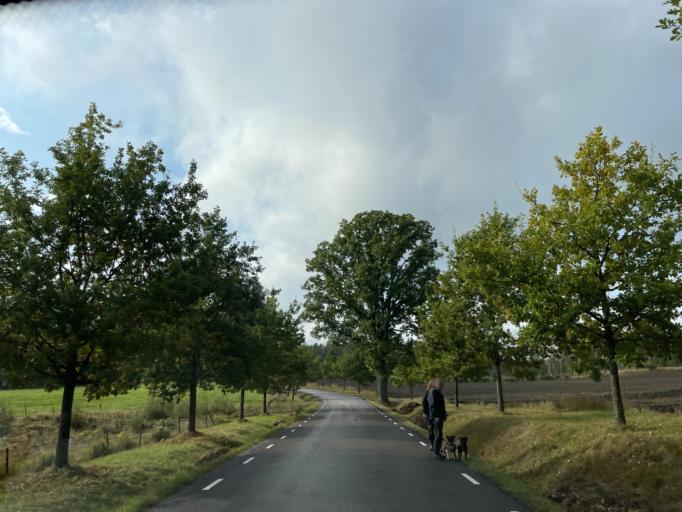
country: SE
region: Vaermland
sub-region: Karlstads Kommun
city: Skattkarr
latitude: 59.4127
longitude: 13.6049
